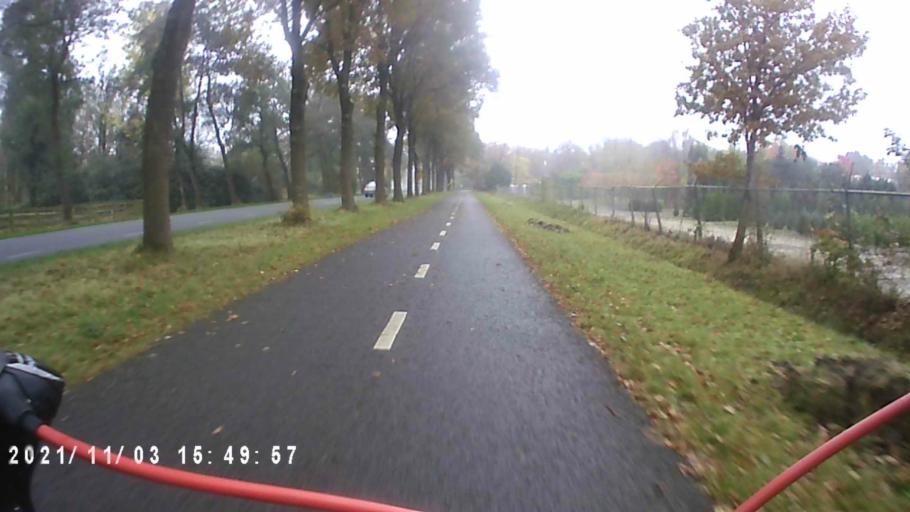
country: NL
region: Groningen
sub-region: Gemeente Leek
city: Leek
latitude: 53.0826
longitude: 6.3371
